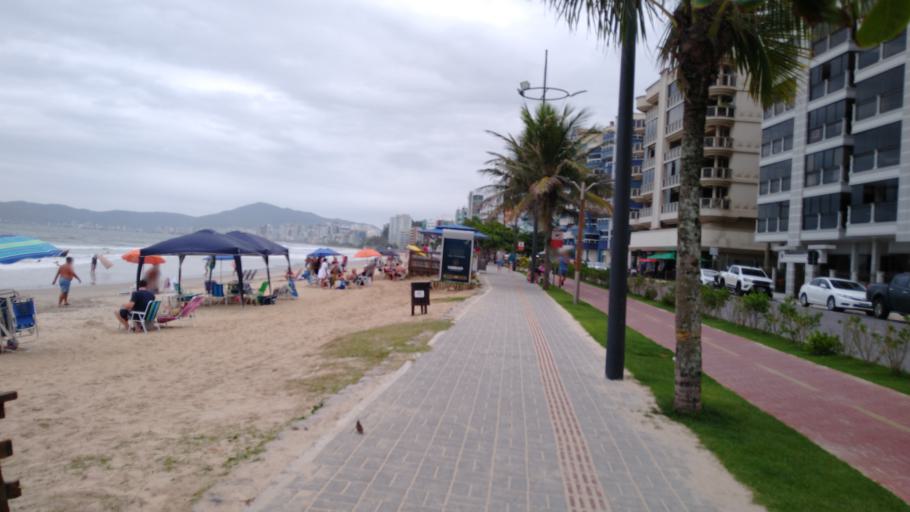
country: BR
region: Santa Catarina
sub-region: Itapema
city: Itapema
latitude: -27.1000
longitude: -48.6140
